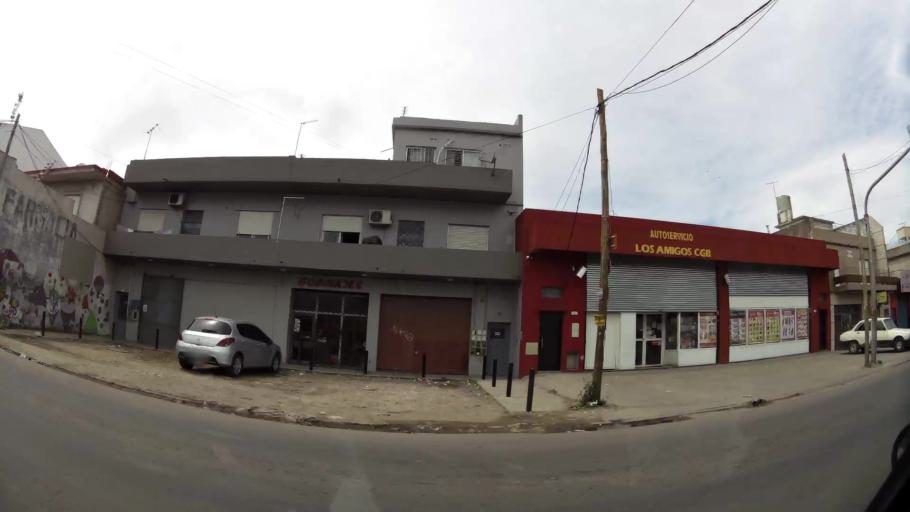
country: AR
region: Buenos Aires
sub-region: Partido de Quilmes
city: Quilmes
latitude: -34.7793
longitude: -58.2653
